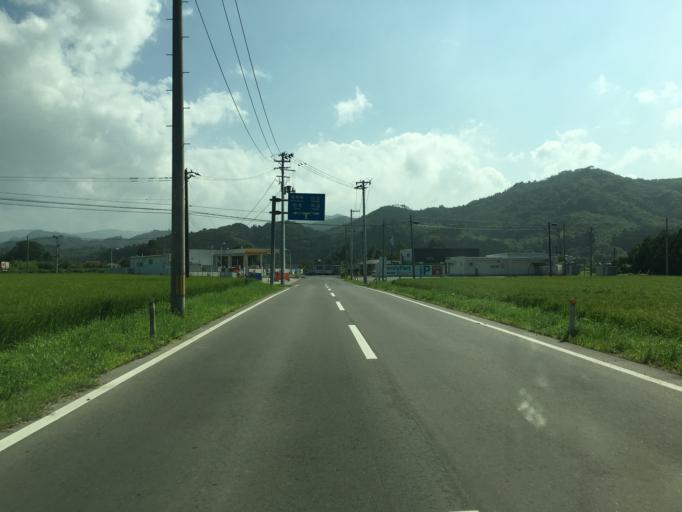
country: JP
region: Miyagi
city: Marumori
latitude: 37.8911
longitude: 140.8128
